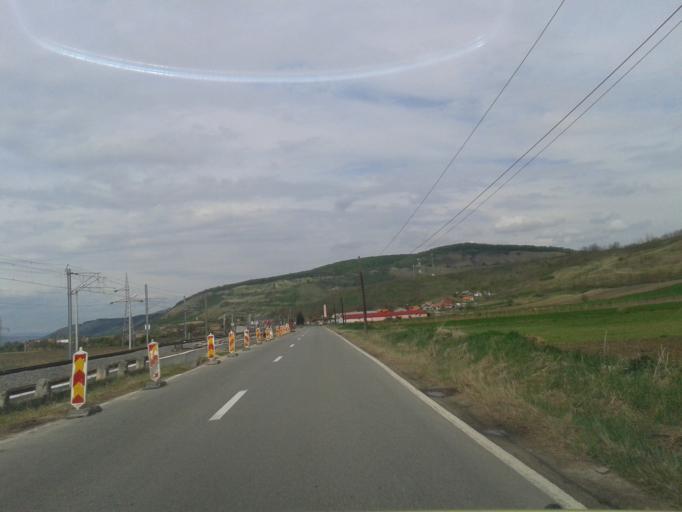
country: RO
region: Alba
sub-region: Comuna Valea Lunga
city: Valea Lunga
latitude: 46.1115
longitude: 24.0446
